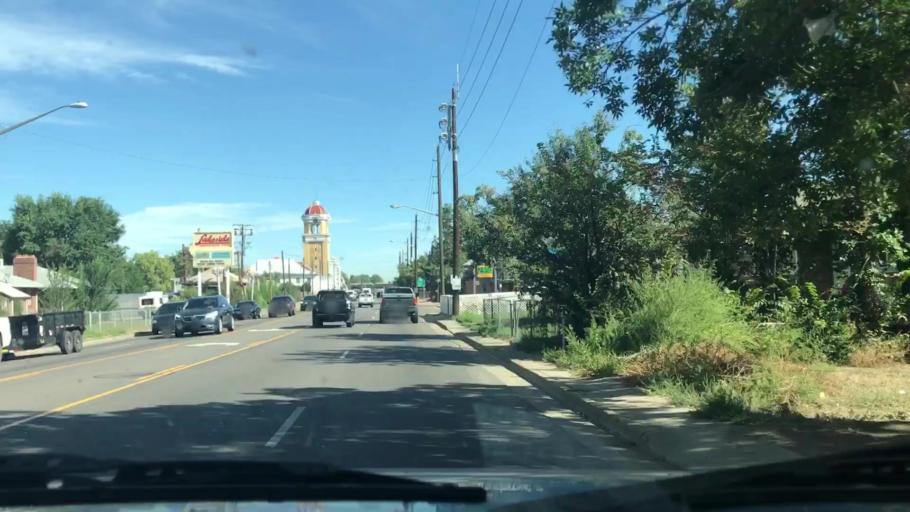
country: US
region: Colorado
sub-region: Jefferson County
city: Wheat Ridge
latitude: 39.7773
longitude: -105.0532
